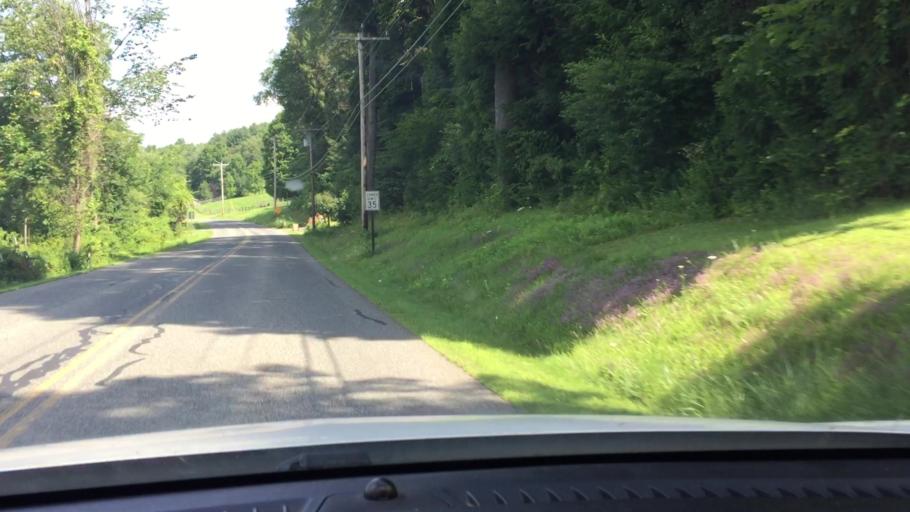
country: US
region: Massachusetts
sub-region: Berkshire County
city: Lee
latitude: 42.2369
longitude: -73.1946
